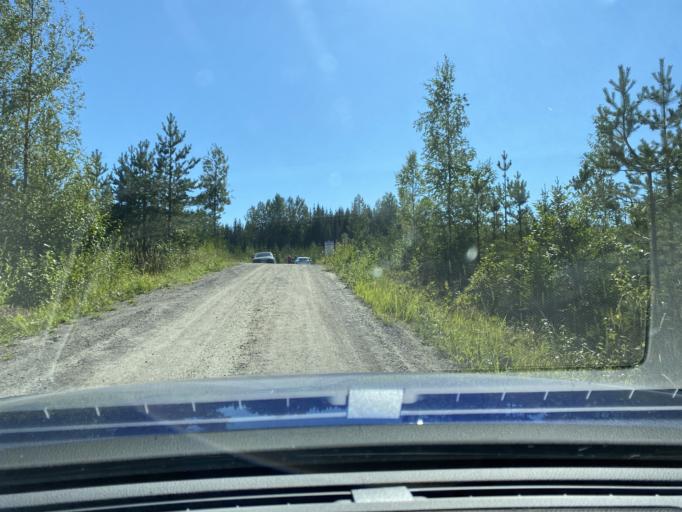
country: FI
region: Central Finland
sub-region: Jaemsae
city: Jaemsae
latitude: 61.8306
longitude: 25.3658
